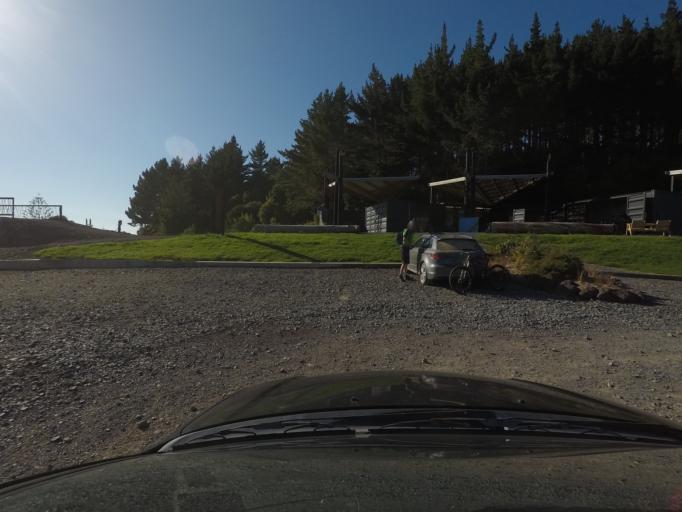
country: NZ
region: Northland
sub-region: Far North District
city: Paihia
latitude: -35.2527
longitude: 174.0705
